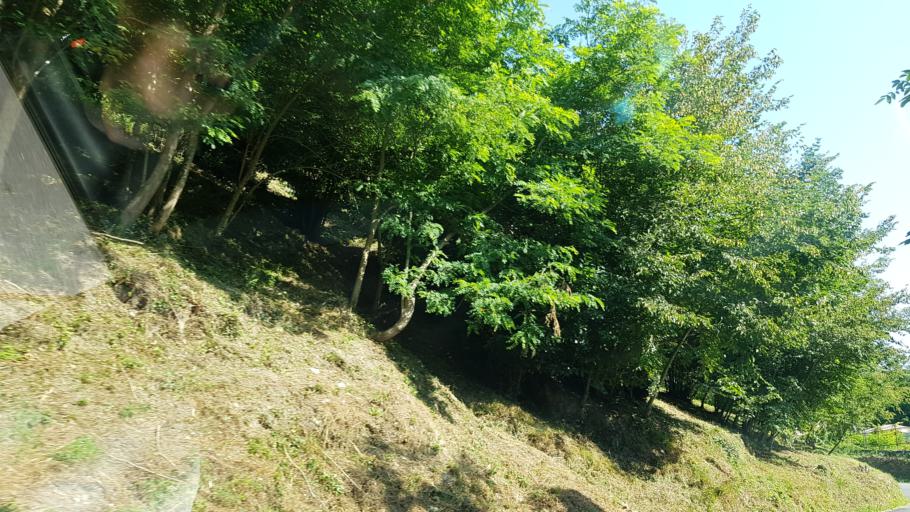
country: IT
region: Liguria
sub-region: Provincia di Genova
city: Serra Ricco
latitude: 44.5174
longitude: 8.9394
